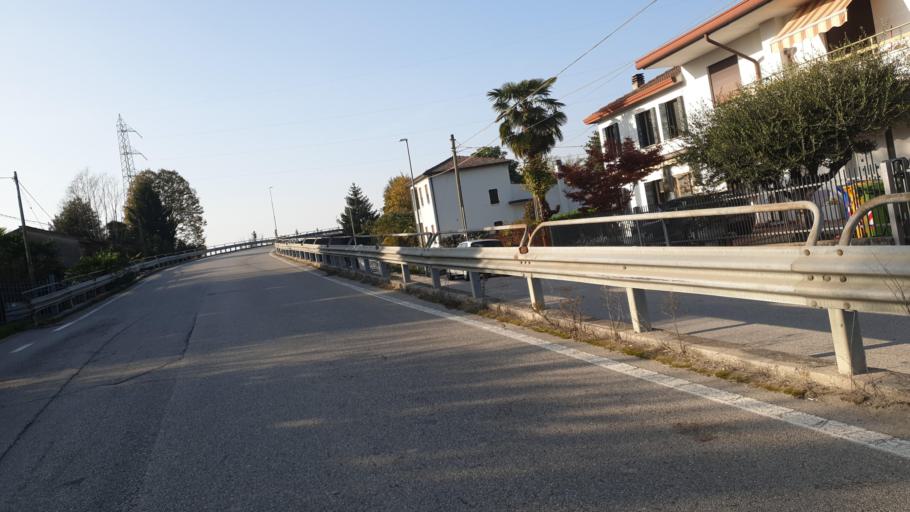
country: IT
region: Veneto
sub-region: Provincia di Venezia
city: Tombelle
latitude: 45.3838
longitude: 11.9857
